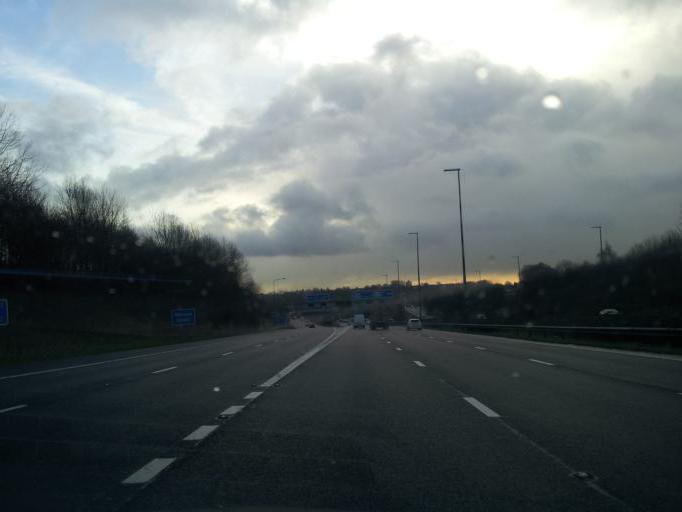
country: GB
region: England
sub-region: Manchester
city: Crumpsall
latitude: 53.5428
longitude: -2.2435
